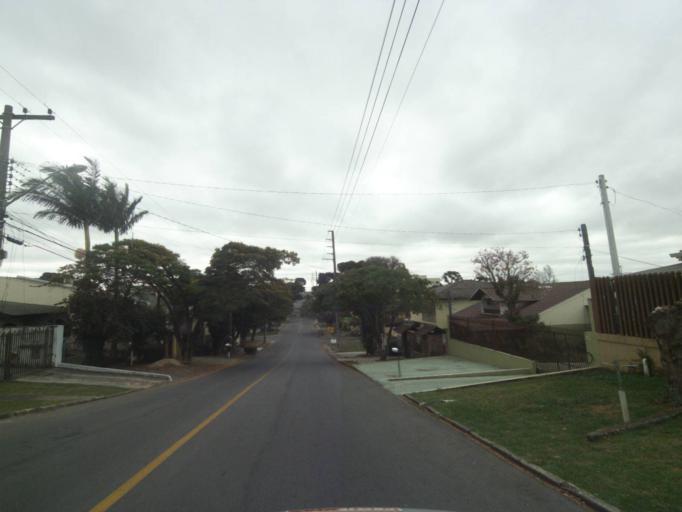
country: BR
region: Parana
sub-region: Pinhais
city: Pinhais
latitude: -25.4803
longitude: -49.2288
